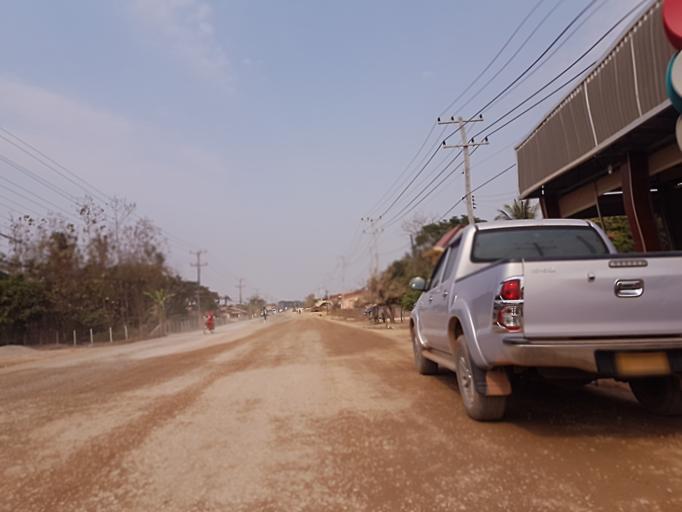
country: TH
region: Nong Khai
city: Nong Khai
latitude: 17.9039
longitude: 102.7592
